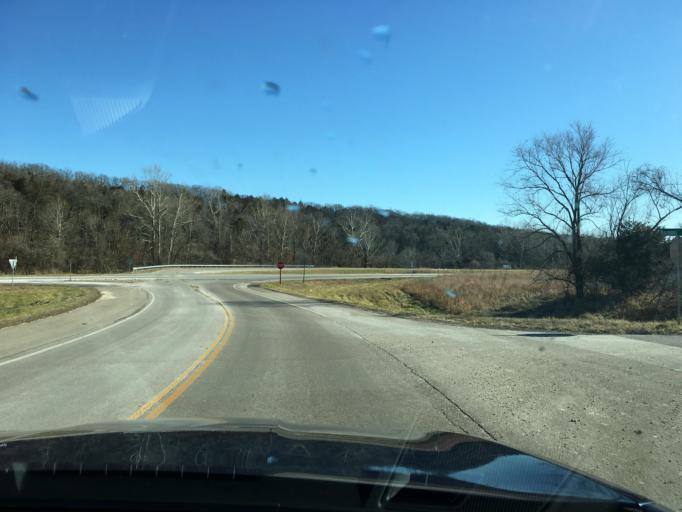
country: US
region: Missouri
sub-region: Jefferson County
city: De Soto
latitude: 38.1518
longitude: -90.5412
